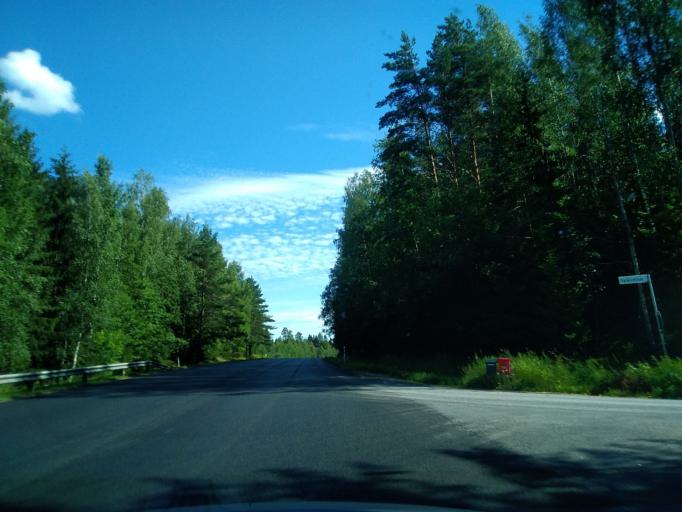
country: FI
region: Haeme
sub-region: Haemeenlinna
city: Haemeenlinna
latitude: 60.9527
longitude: 24.4078
